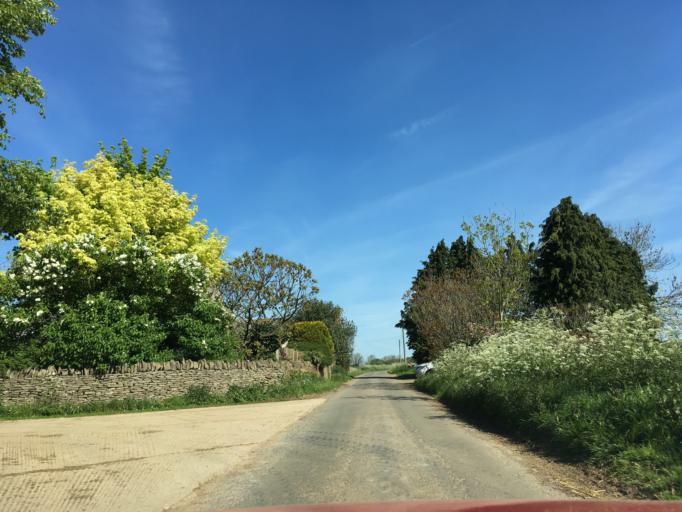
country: GB
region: England
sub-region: Wiltshire
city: Luckington
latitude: 51.6241
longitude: -2.2582
